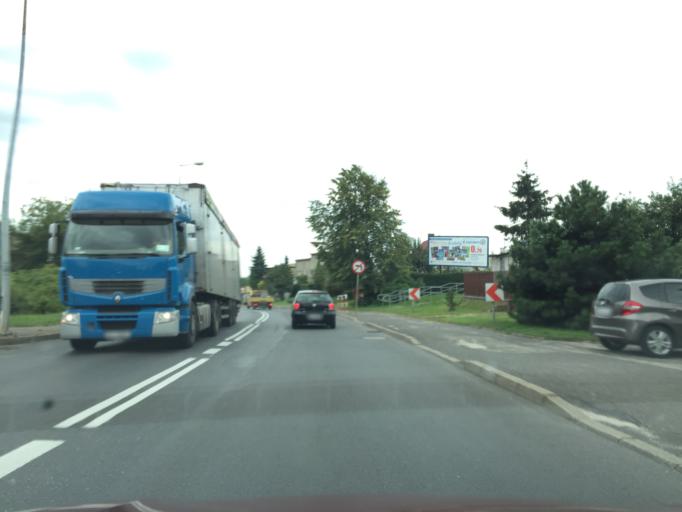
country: PL
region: Greater Poland Voivodeship
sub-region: Kalisz
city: Kalisz
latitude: 51.7746
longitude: 18.0892
